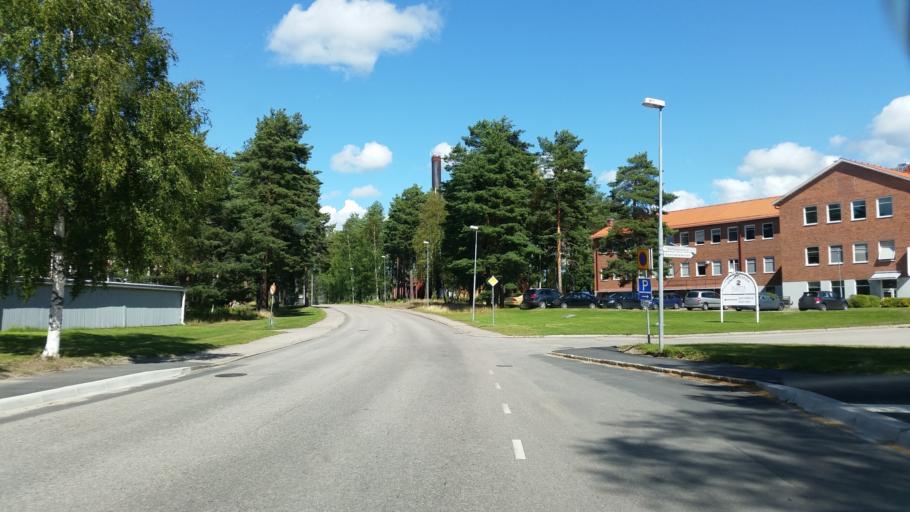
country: SE
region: Gaevleborg
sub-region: Ljusdals Kommun
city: Ljusdal
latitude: 61.8301
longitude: 16.1166
